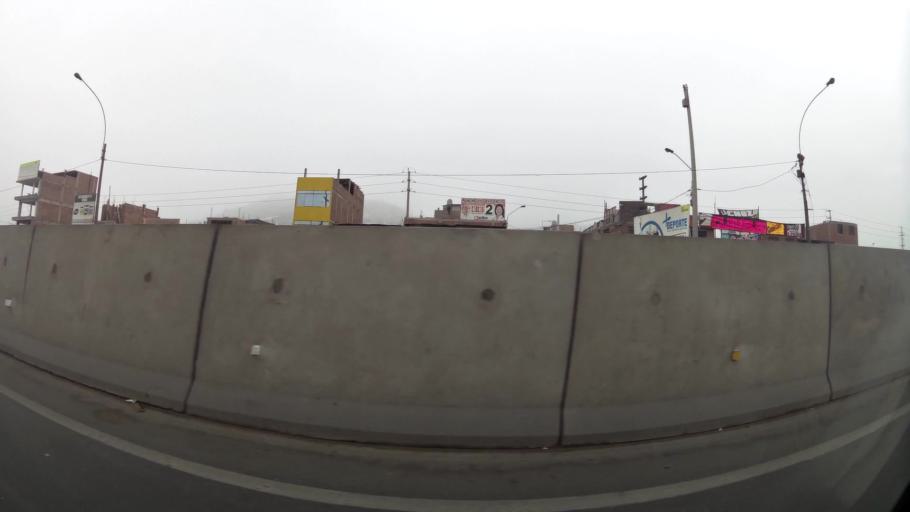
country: PE
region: Lima
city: Ventanilla
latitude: -11.8296
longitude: -77.1183
